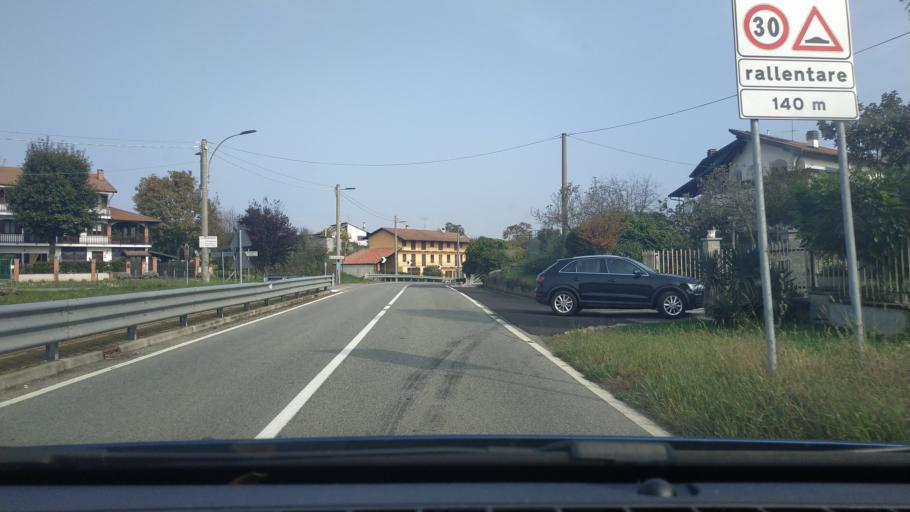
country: IT
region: Piedmont
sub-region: Provincia di Torino
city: Scarmagno
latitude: 45.3636
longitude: 7.8427
